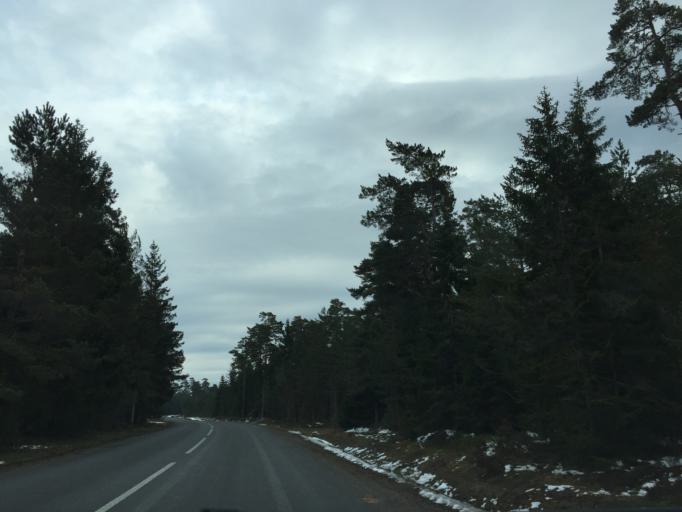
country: EE
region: Saare
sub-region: Kuressaare linn
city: Kuressaare
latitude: 58.4327
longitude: 22.0682
